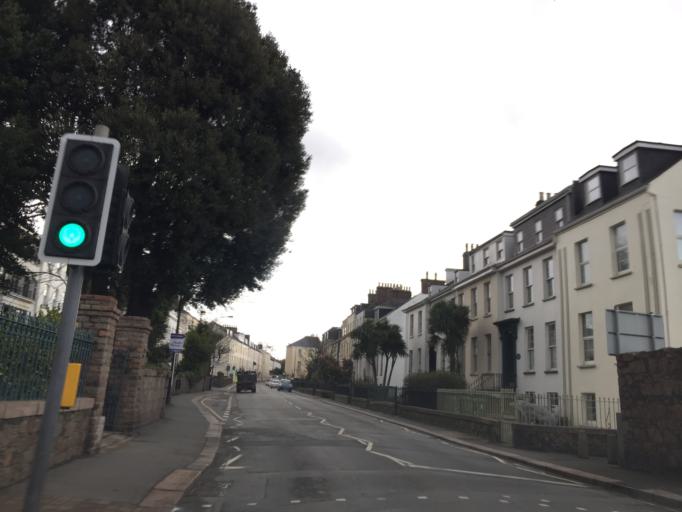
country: JE
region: St Helier
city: Saint Helier
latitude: 49.1928
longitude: -2.1079
